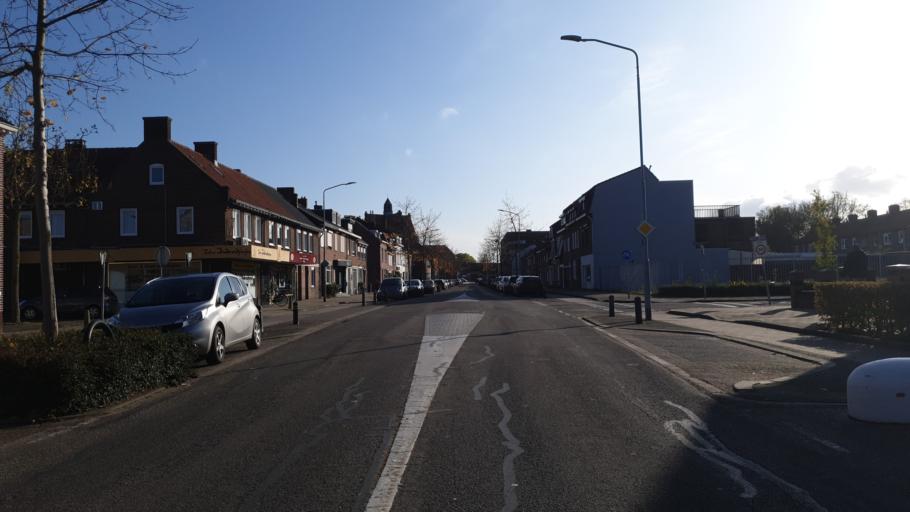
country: NL
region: Limburg
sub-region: Gemeente Venlo
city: Venlo
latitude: 51.3804
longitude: 6.1795
